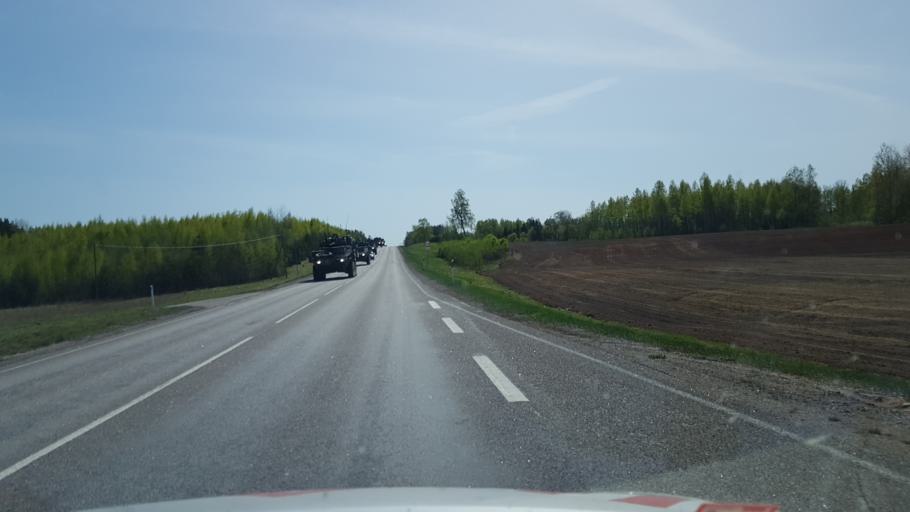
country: EE
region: Tartu
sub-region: Elva linn
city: Elva
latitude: 58.0805
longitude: 26.2080
